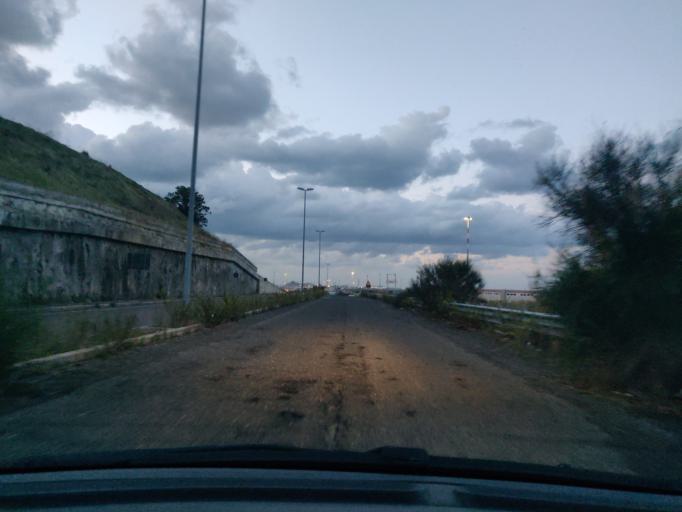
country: IT
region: Latium
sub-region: Citta metropolitana di Roma Capitale
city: Aurelia
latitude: 42.1264
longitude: 11.7780
